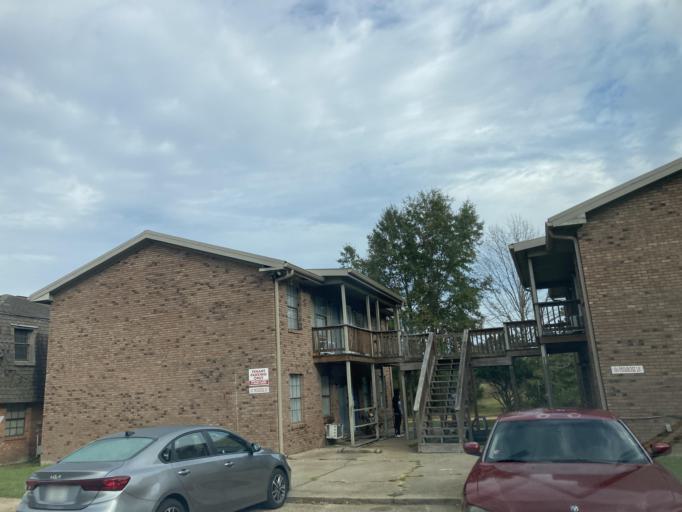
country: US
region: Mississippi
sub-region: Lamar County
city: West Hattiesburg
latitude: 31.3194
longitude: -89.3702
